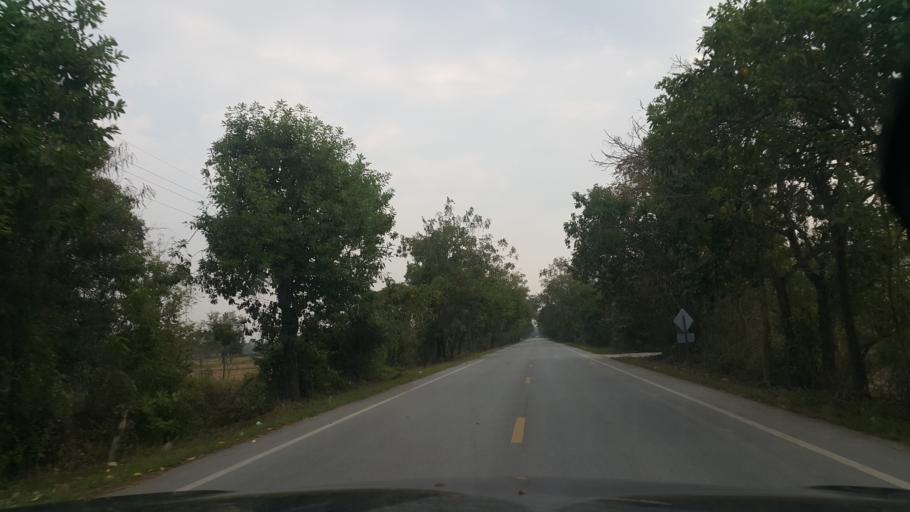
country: TH
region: Sukhothai
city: Si Samrong
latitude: 17.1698
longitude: 99.7165
